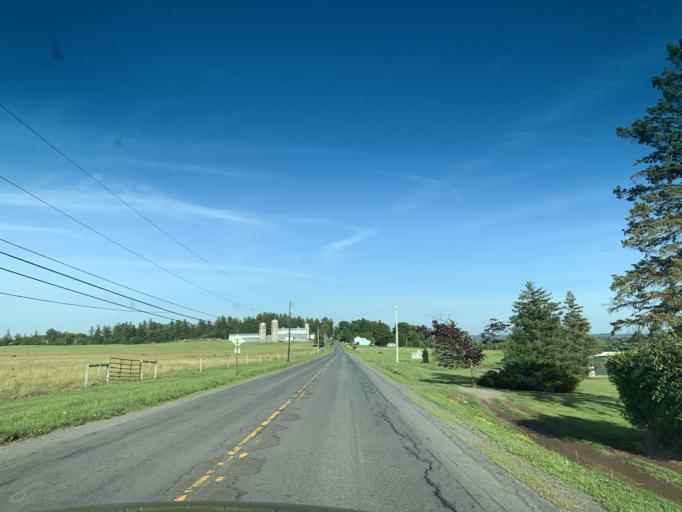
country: US
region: New York
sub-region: Oneida County
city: Clinton
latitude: 43.0530
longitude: -75.4244
